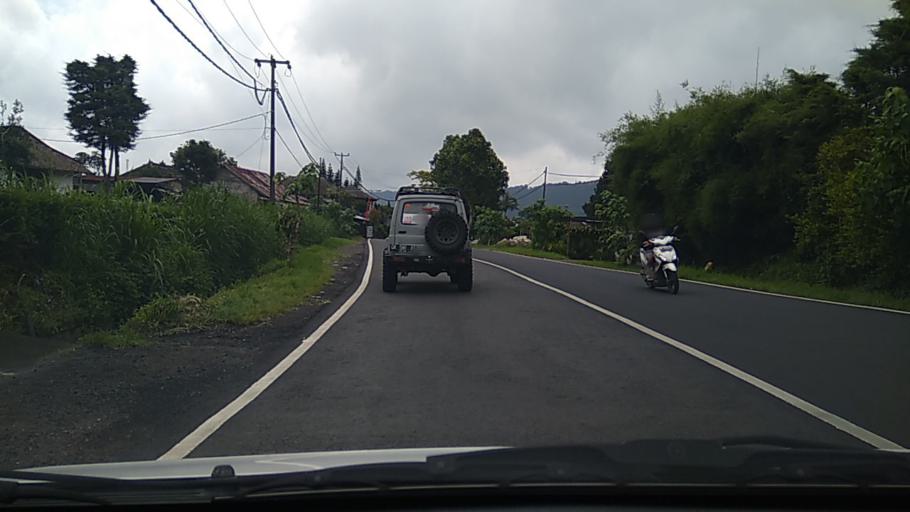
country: ID
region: Bali
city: Munduk
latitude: -8.2516
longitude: 115.1548
